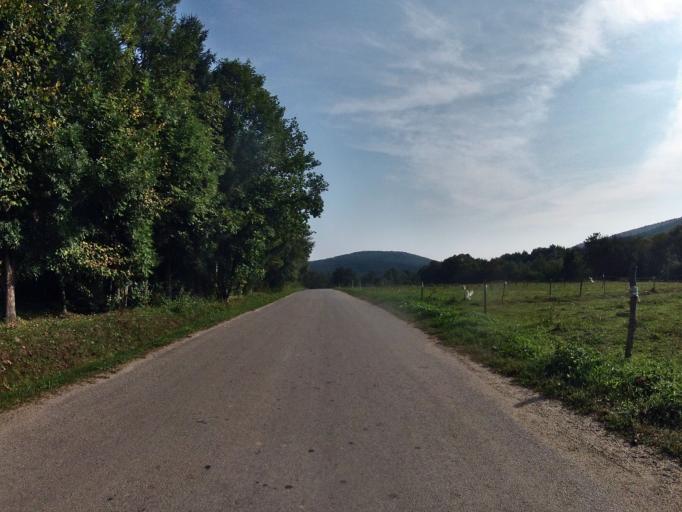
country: PL
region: Subcarpathian Voivodeship
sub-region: Powiat jasielski
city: Krempna
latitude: 49.5377
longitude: 21.5489
